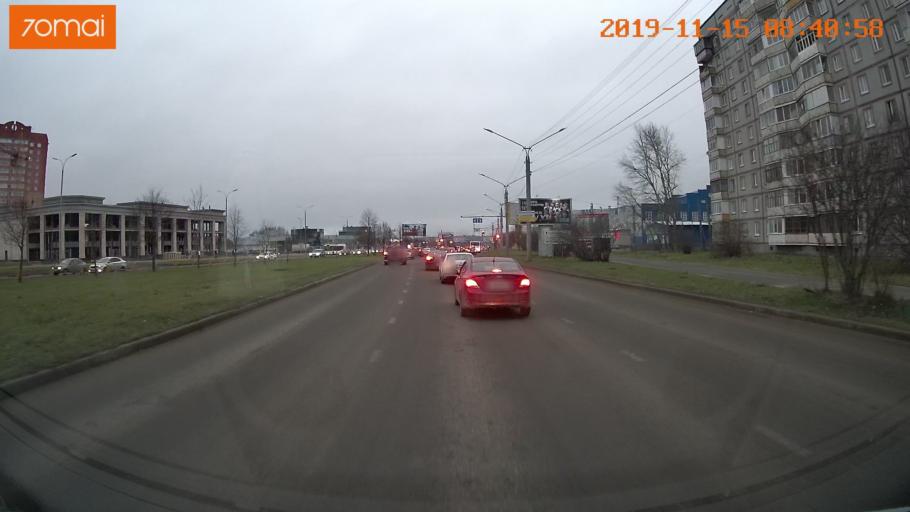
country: RU
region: Vologda
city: Cherepovets
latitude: 59.0968
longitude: 37.9124
